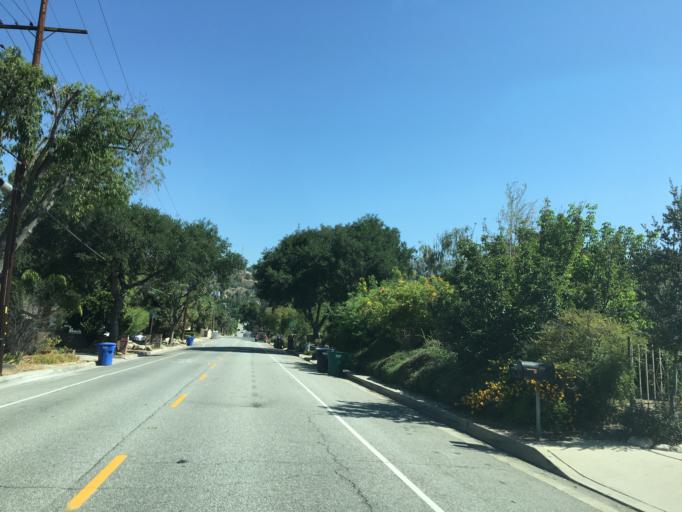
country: US
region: California
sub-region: Los Angeles County
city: Claremont
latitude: 34.1234
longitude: -117.7290
